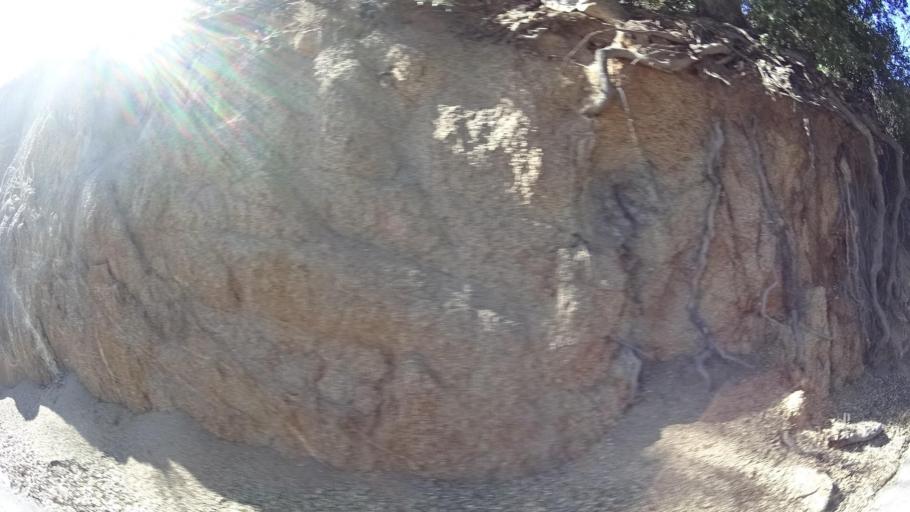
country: US
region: California
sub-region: Riverside County
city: Aguanga
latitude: 33.3739
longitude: -116.7161
